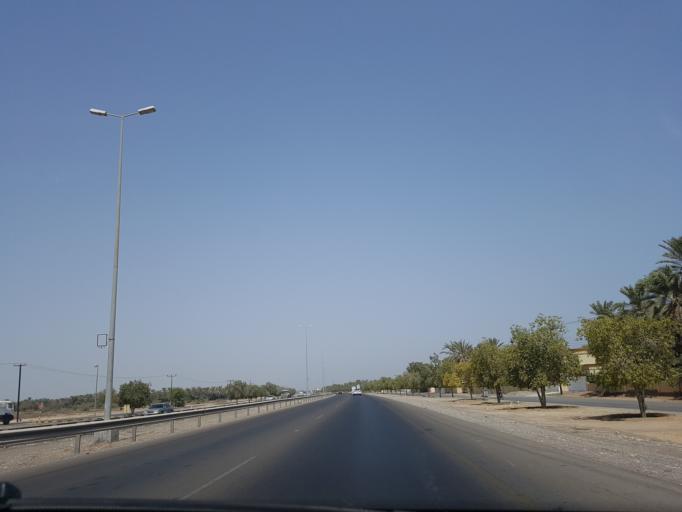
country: OM
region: Al Batinah
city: Al Khaburah
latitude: 24.0369
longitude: 57.0165
